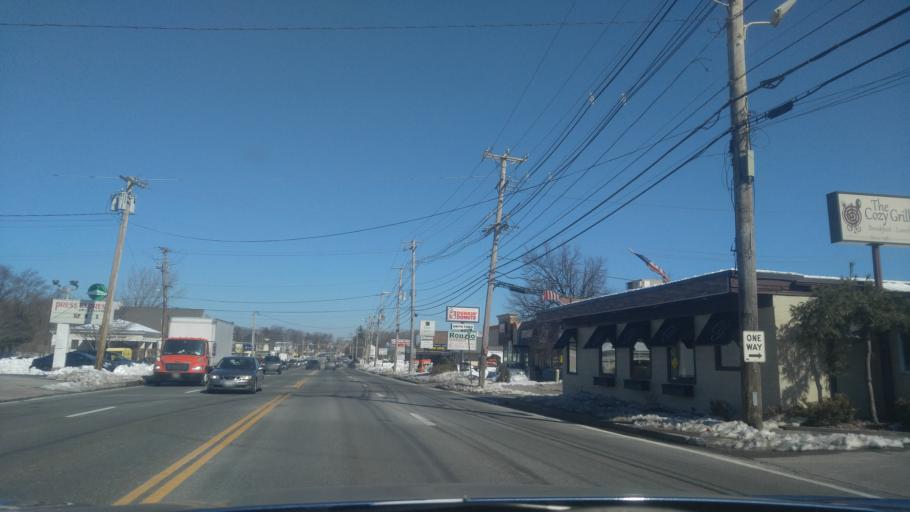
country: US
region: Rhode Island
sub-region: Providence County
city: Cranston
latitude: 41.7639
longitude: -71.4049
